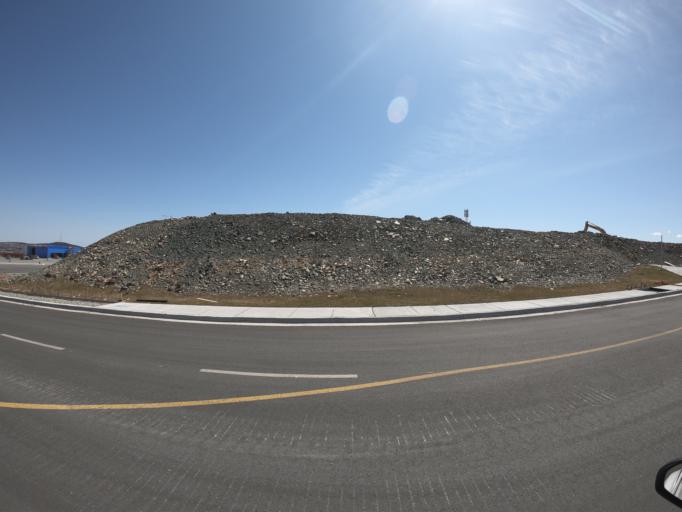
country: CA
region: Newfoundland and Labrador
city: Mount Pearl
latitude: 47.5085
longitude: -52.8328
